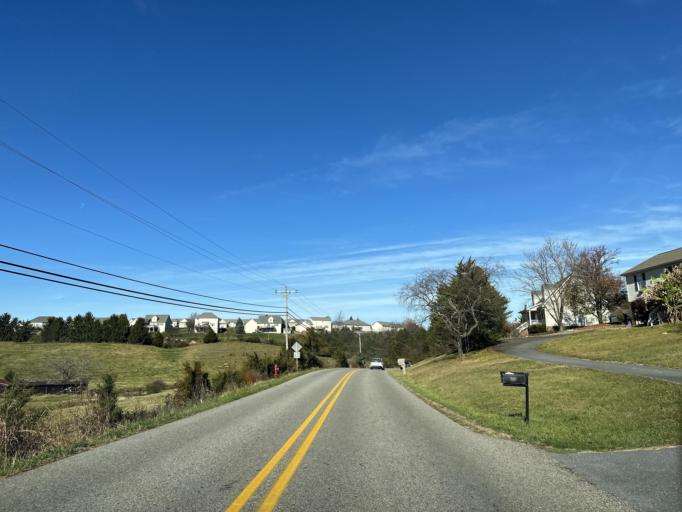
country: US
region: Virginia
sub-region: Augusta County
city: Fishersville
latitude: 38.1048
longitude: -78.9627
